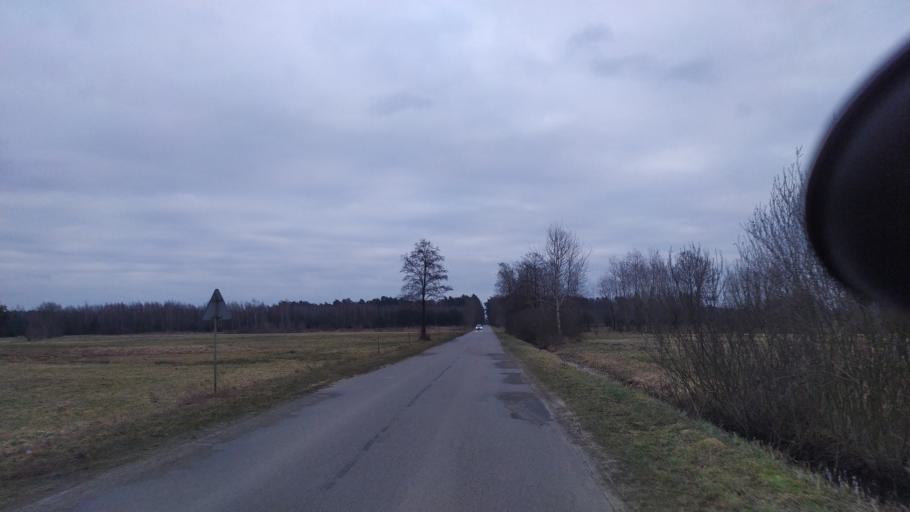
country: PL
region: Lublin Voivodeship
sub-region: Powiat lubartowski
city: Abramow
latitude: 51.4249
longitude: 22.3155
